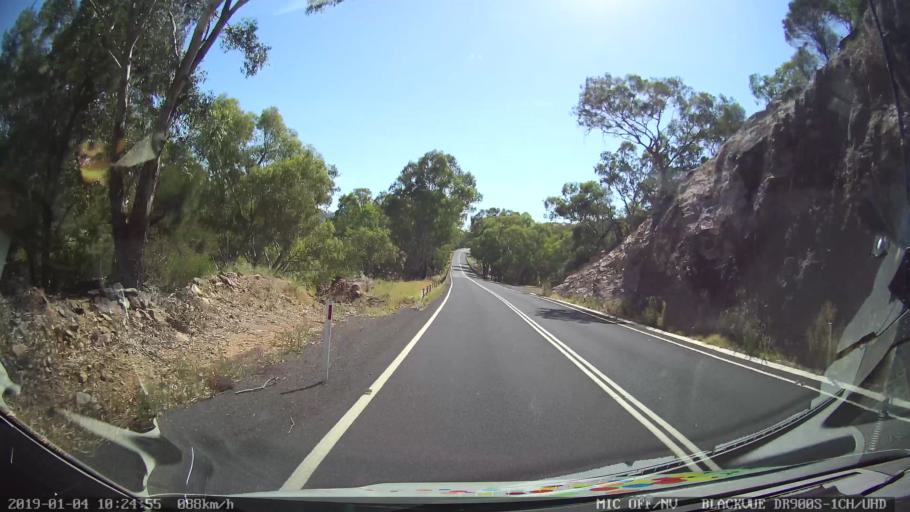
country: AU
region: New South Wales
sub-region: Cabonne
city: Canowindra
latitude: -33.3693
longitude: 148.5625
